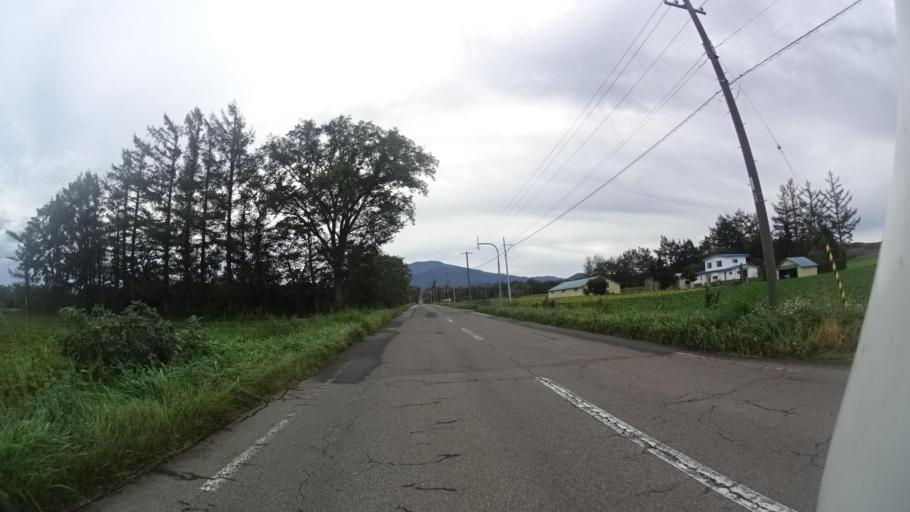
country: JP
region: Hokkaido
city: Abashiri
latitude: 43.8730
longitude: 144.7138
